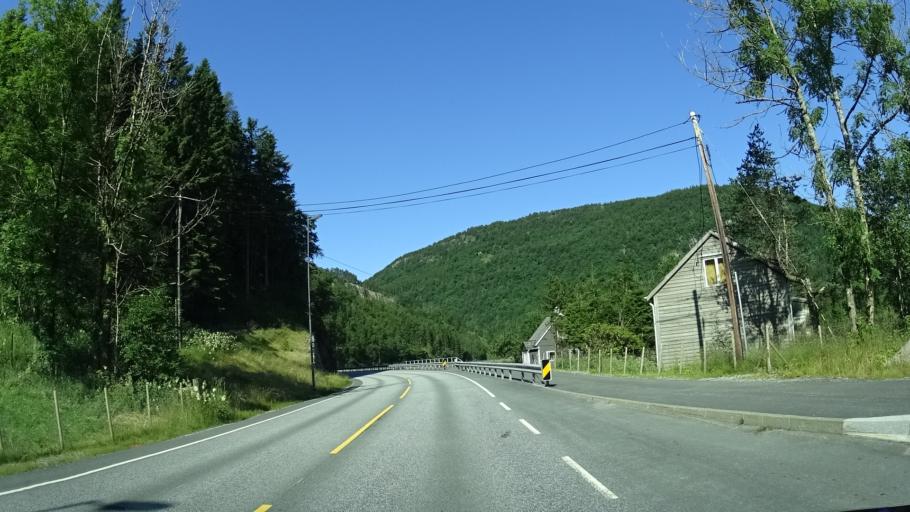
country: NO
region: Hordaland
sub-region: Samnanger
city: Tysse
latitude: 60.3787
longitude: 5.8010
